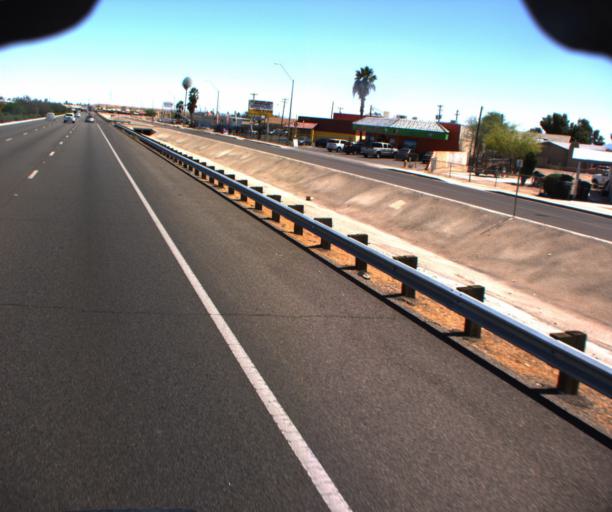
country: US
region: Arizona
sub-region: Maricopa County
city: El Mirage
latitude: 33.6141
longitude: -112.3189
